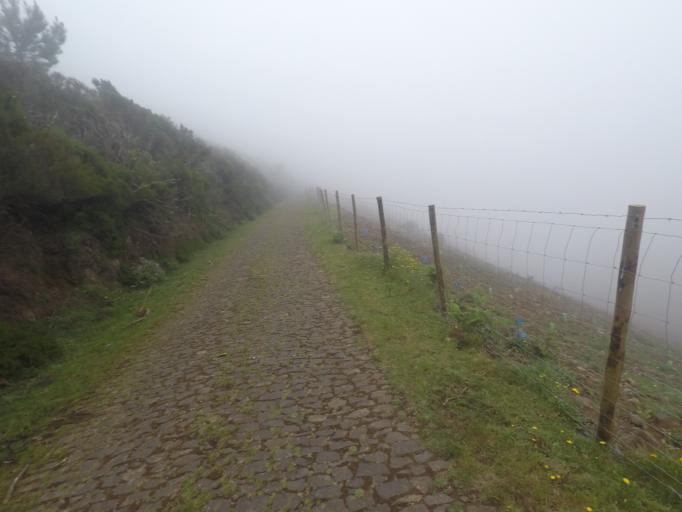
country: PT
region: Madeira
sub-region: Calheta
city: Arco da Calheta
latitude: 32.7347
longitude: -17.0965
